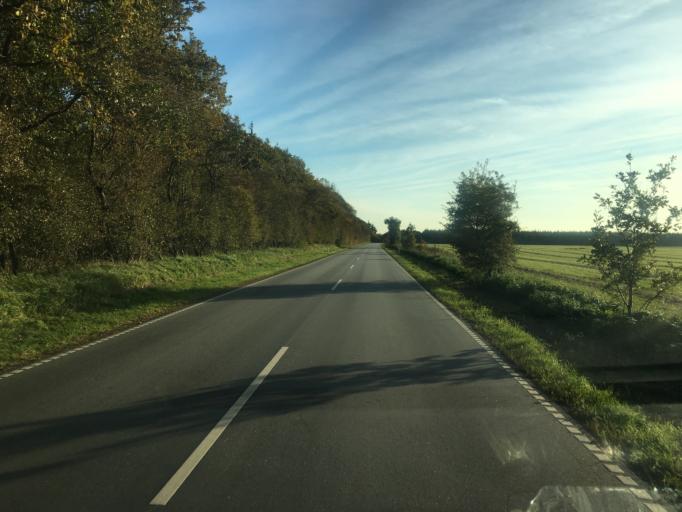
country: DE
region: Schleswig-Holstein
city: Bramstedtlund
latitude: 54.8894
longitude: 9.0919
